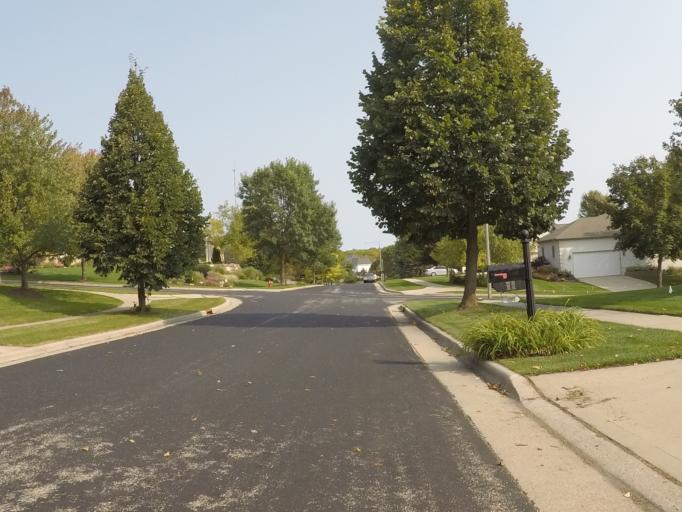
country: US
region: Wisconsin
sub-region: Dane County
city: Verona
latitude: 43.0344
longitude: -89.5369
